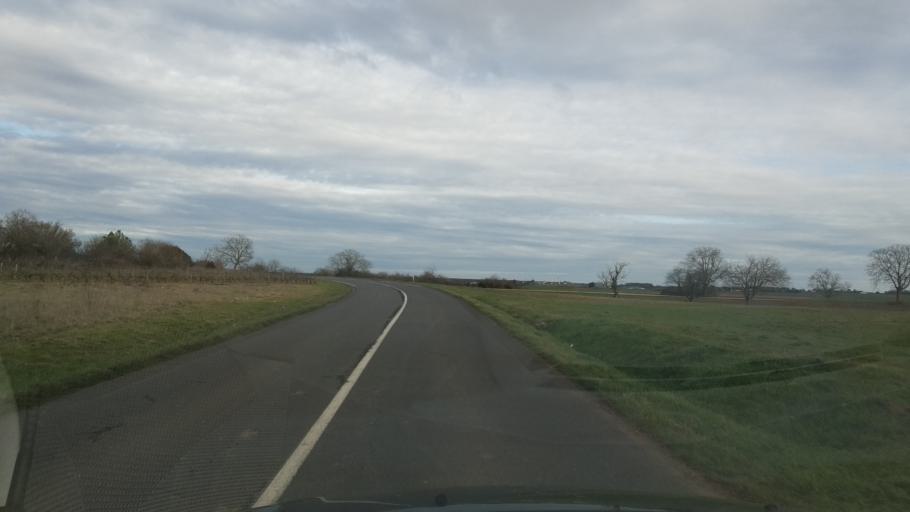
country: FR
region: Poitou-Charentes
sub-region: Departement de la Vienne
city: Saint-Georges-les-Baillargeaux
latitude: 46.6625
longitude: 0.3970
